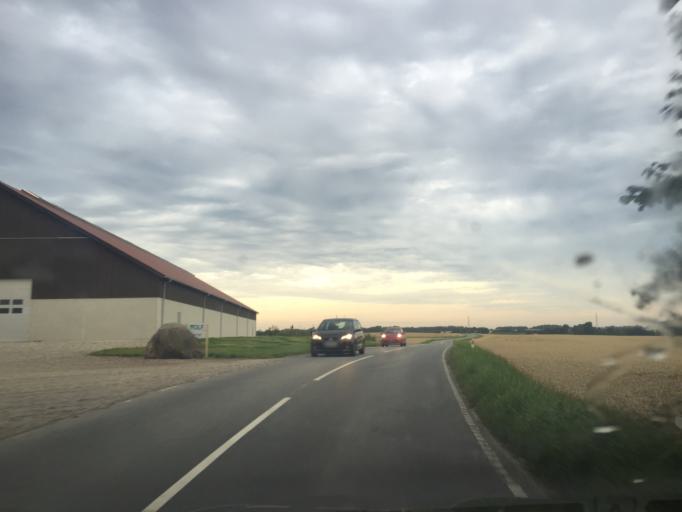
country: DK
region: Capital Region
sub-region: Egedal Kommune
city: Vekso
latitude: 55.6926
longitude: 12.2440
